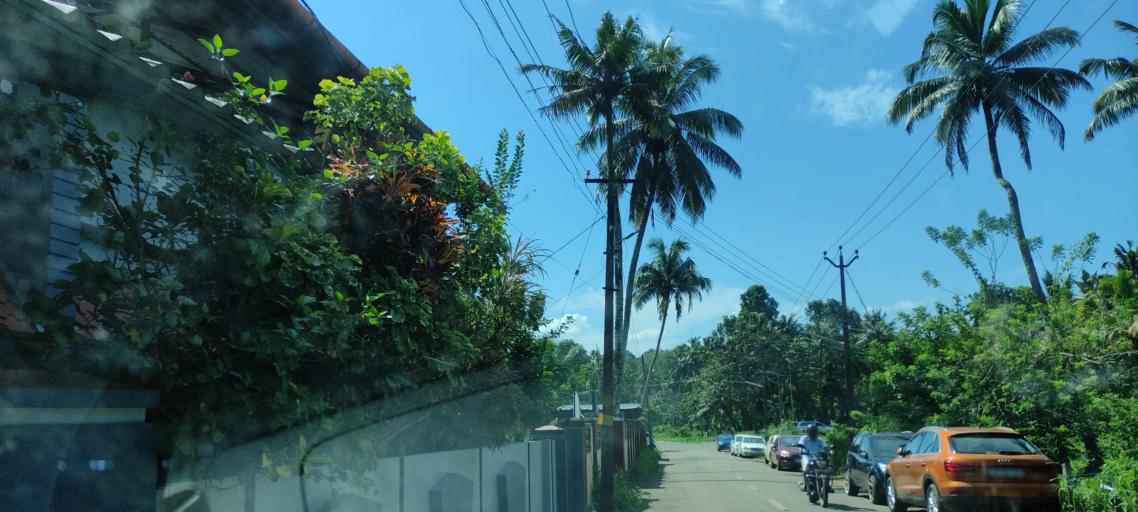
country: IN
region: Kerala
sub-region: Pattanamtitta
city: Adur
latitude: 9.1564
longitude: 76.7274
